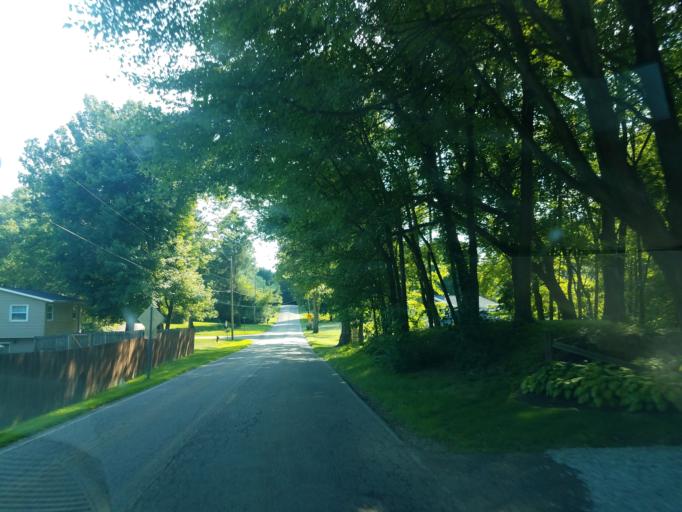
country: US
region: Ohio
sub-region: Stark County
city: Uniontown
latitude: 40.9730
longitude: -81.4141
